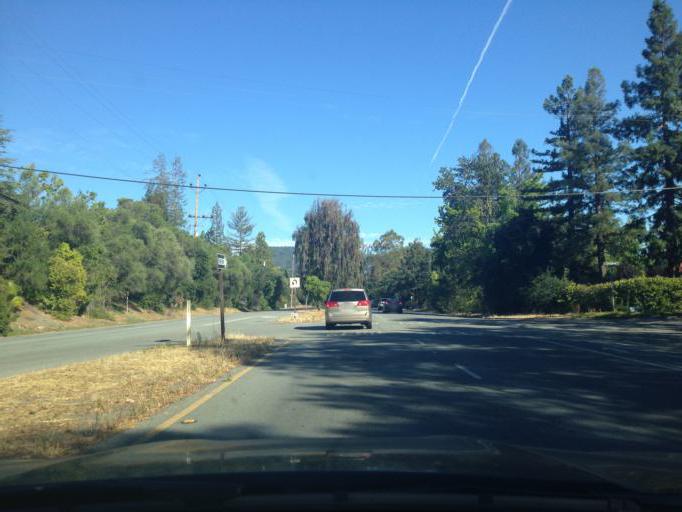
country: US
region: California
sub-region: Santa Clara County
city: Monte Sereno
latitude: 37.2367
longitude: -121.9929
